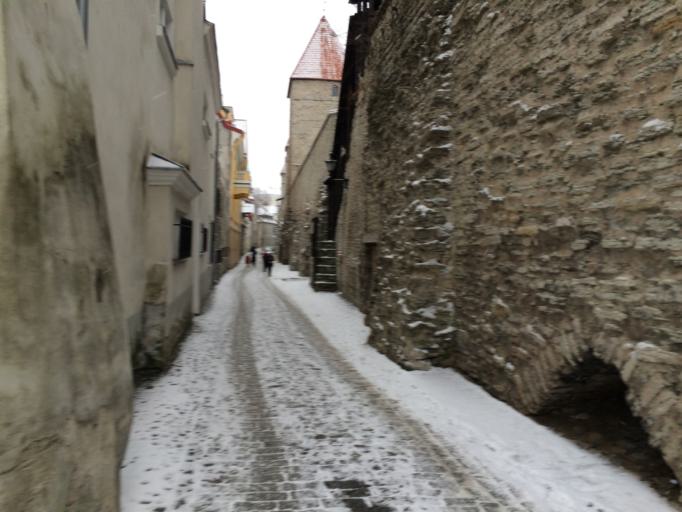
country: EE
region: Harju
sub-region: Tallinna linn
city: Tallinn
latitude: 59.4420
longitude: 24.7471
